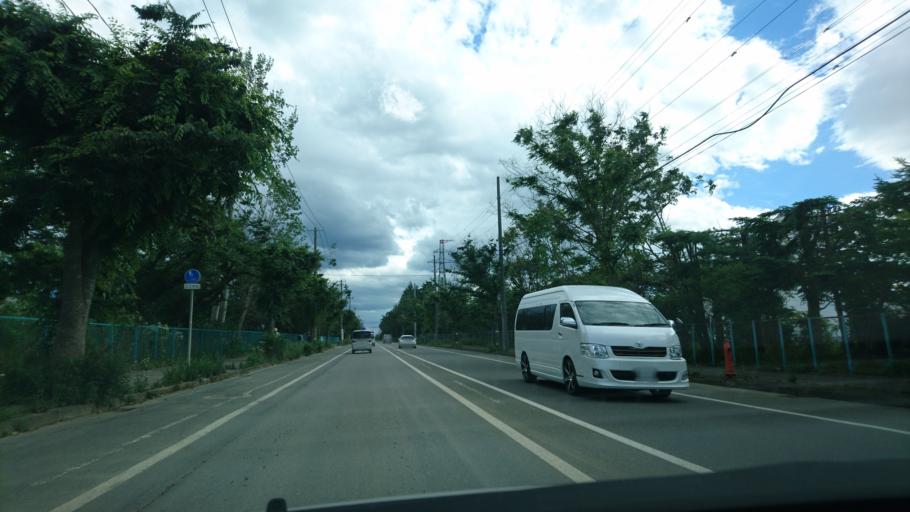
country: JP
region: Iwate
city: Hanamaki
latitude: 39.3380
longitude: 141.1285
